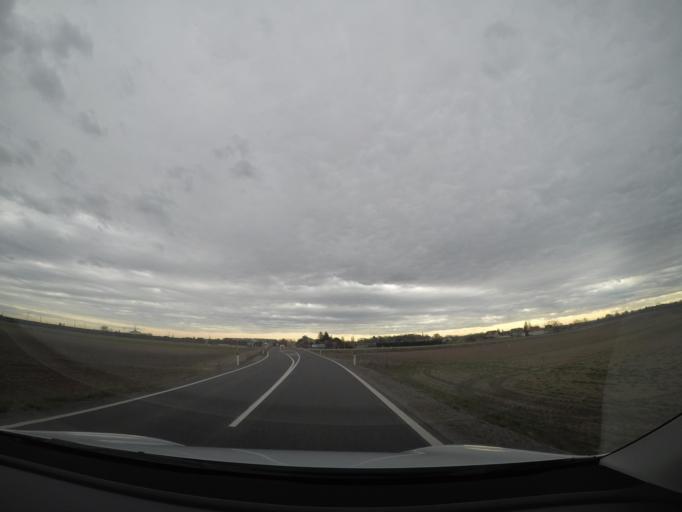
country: AT
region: Lower Austria
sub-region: Politischer Bezirk Modling
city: Achau
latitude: 48.0812
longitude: 16.3717
